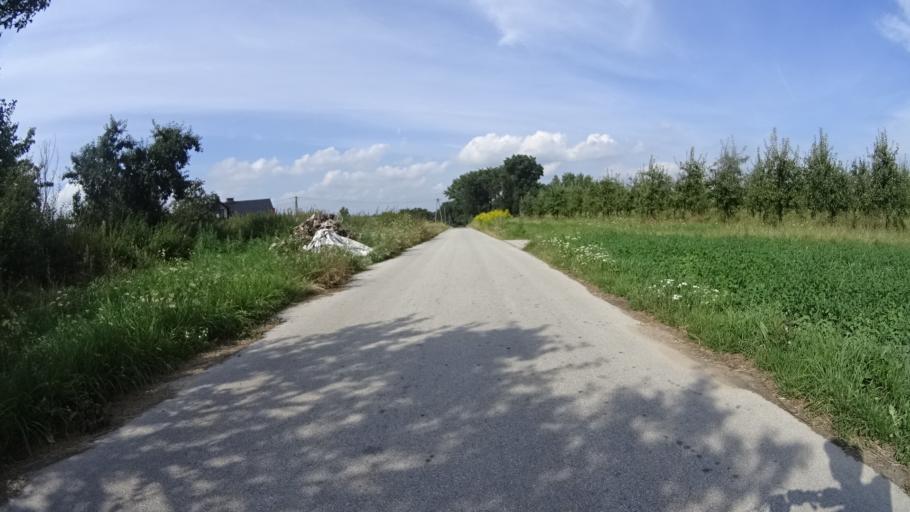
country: PL
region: Masovian Voivodeship
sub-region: Powiat grojecki
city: Goszczyn
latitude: 51.6966
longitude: 20.8477
